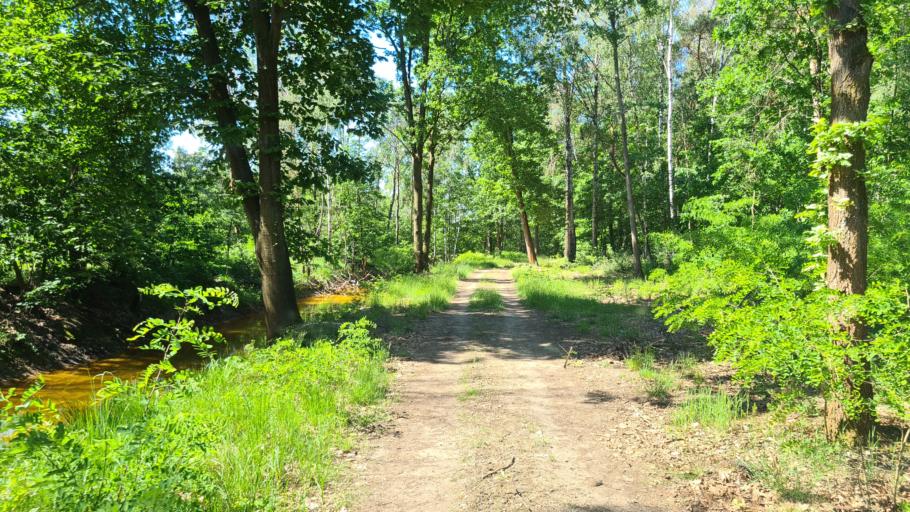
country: DE
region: Brandenburg
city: Plessa
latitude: 51.4715
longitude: 13.6550
